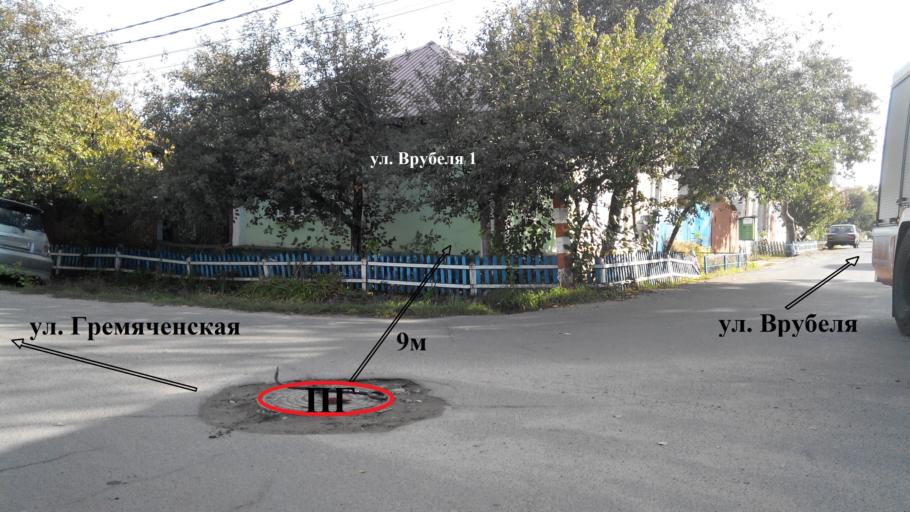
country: RU
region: Voronezj
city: Voronezh
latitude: 51.6245
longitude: 39.1741
